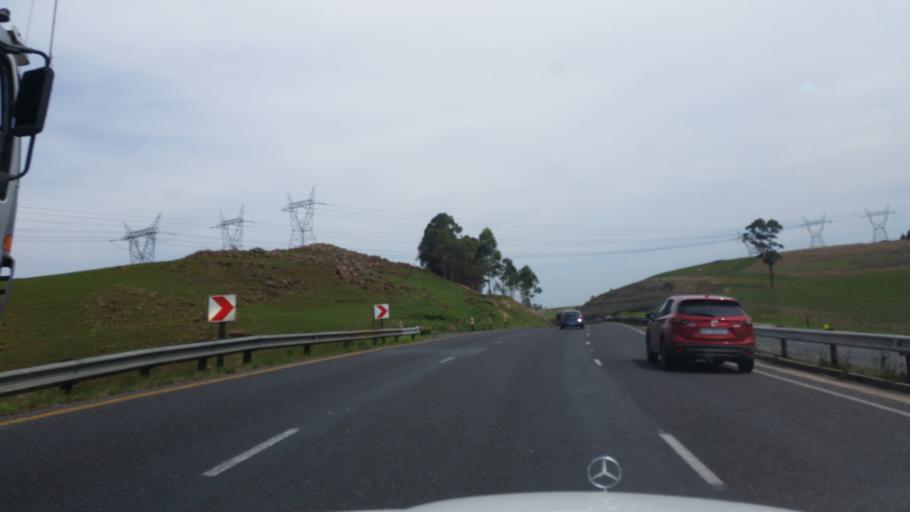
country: ZA
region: KwaZulu-Natal
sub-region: uMgungundlovu District Municipality
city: Howick
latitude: -29.4413
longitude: 30.1756
